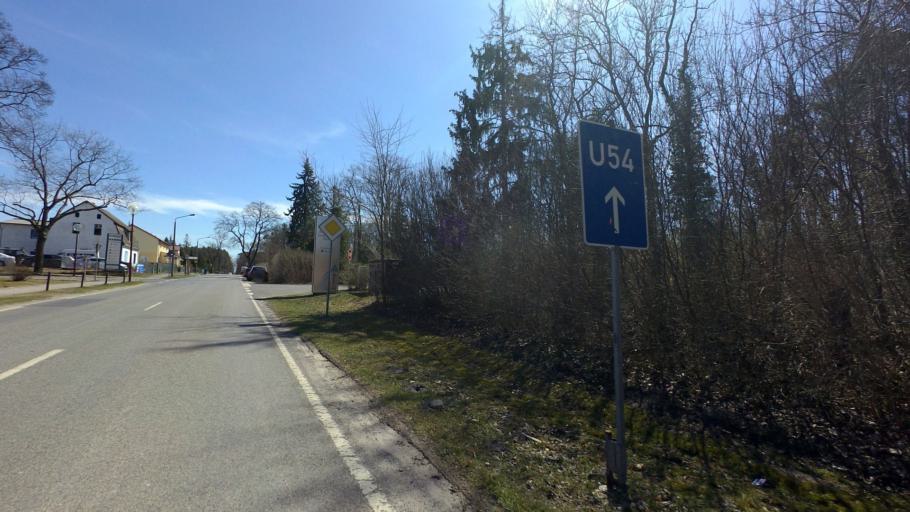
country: DE
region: Brandenburg
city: Teupitz
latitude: 52.1309
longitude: 13.6226
